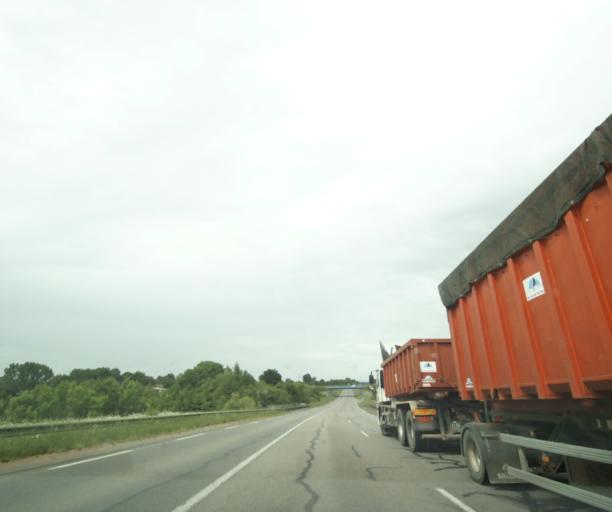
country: FR
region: Poitou-Charentes
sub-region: Departement des Deux-Sevres
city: Le Tallud
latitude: 46.6361
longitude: -0.2766
